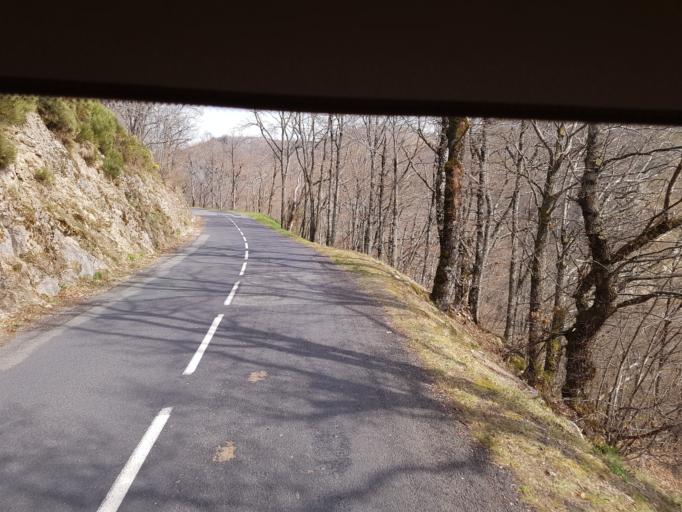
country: FR
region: Languedoc-Roussillon
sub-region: Departement de la Lozere
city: Florac
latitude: 44.3622
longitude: 3.7212
